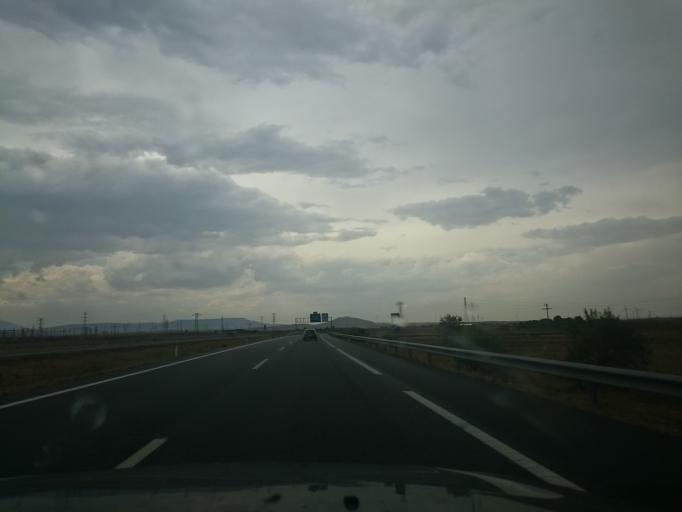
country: ES
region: Aragon
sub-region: Provincia de Zaragoza
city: Gallur
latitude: 41.8481
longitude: -1.3673
